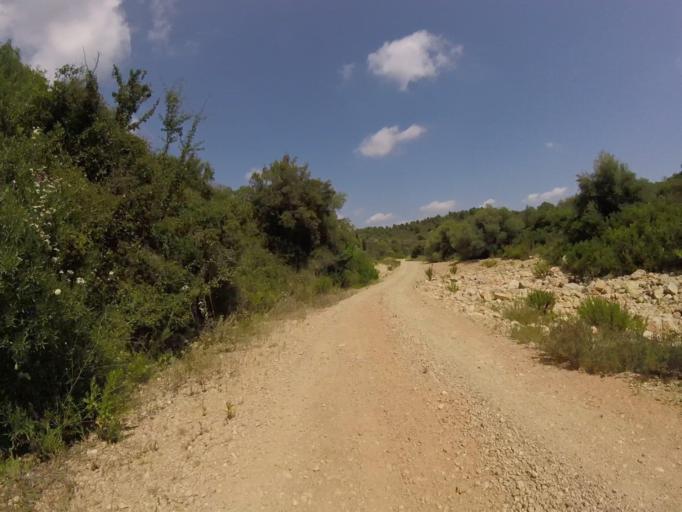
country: ES
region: Valencia
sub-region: Provincia de Castello
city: Torreblanca
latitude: 40.2107
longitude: 0.1395
